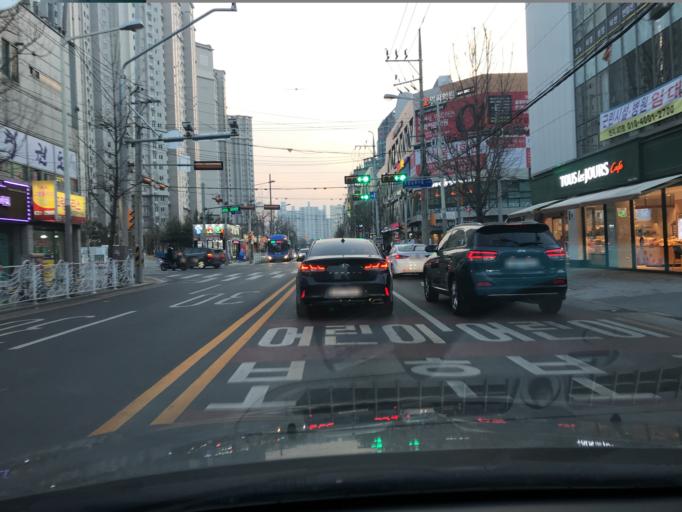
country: KR
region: Daegu
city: Hwawon
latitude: 35.8171
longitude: 128.5182
